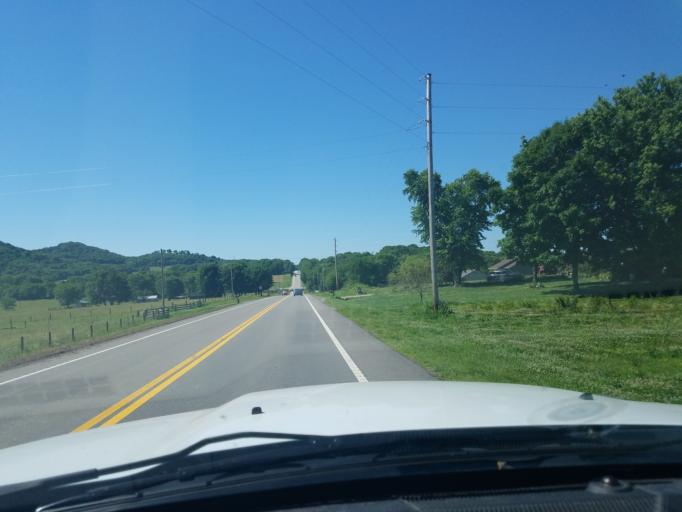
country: US
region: Tennessee
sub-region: Sumner County
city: Westmoreland
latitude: 36.4549
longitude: -86.2672
